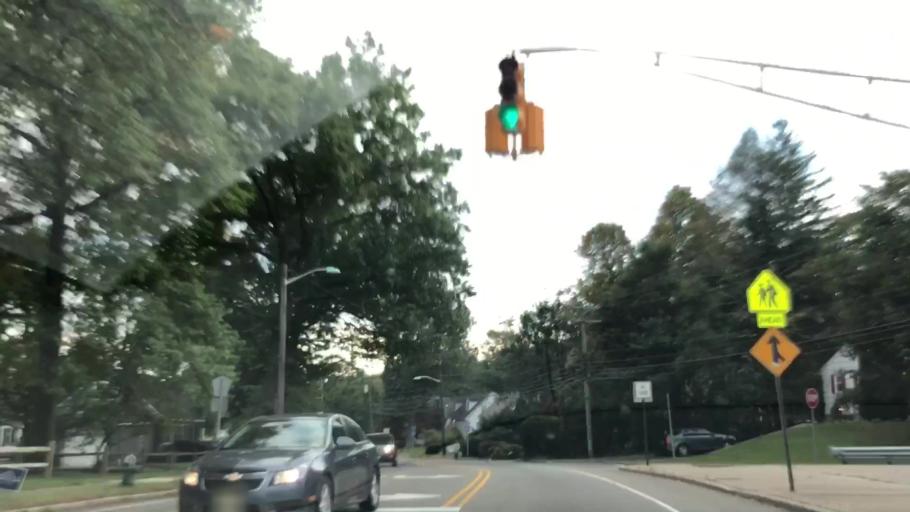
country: US
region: New Jersey
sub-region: Essex County
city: Upper Montclair
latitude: 40.8516
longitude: -74.1940
